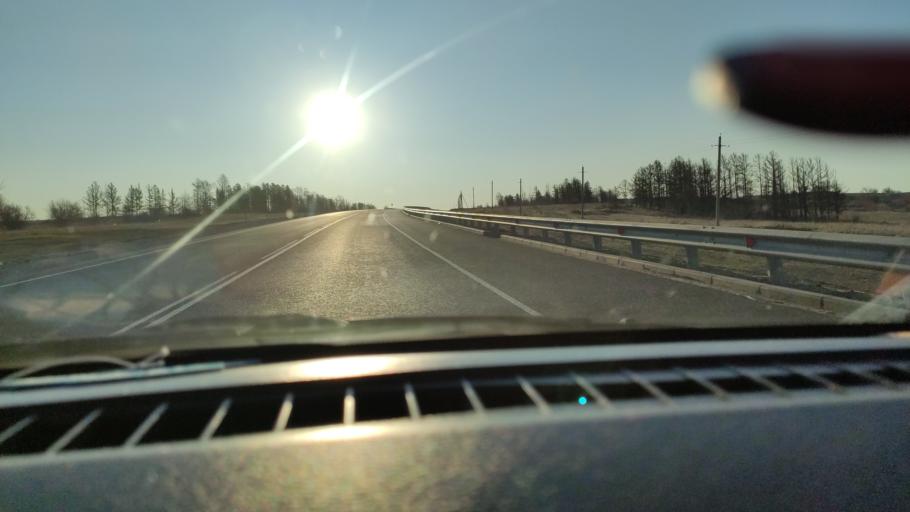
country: RU
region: Saratov
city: Shikhany
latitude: 52.1612
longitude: 47.1065
